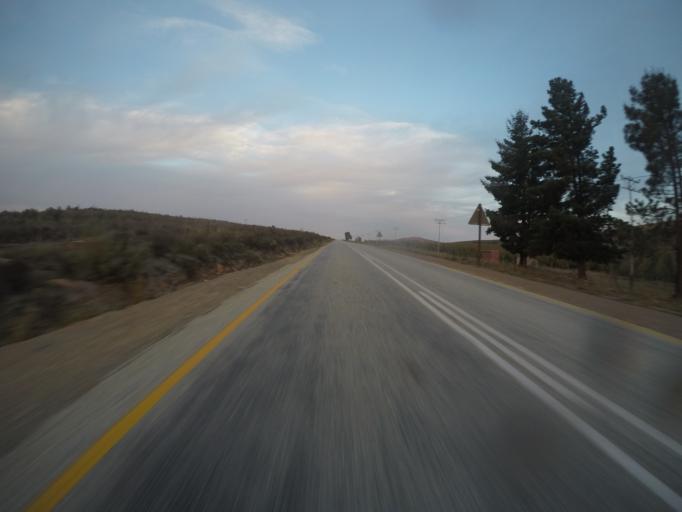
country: ZA
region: Western Cape
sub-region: Eden District Municipality
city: Plettenberg Bay
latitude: -33.7362
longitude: 23.4128
